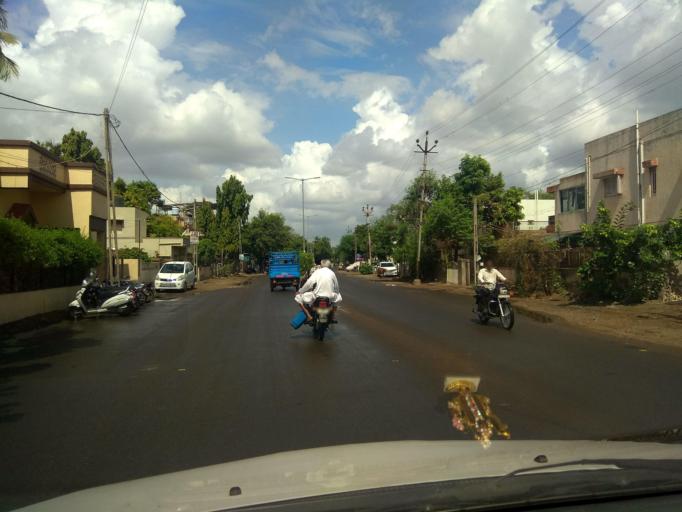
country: IN
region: Gujarat
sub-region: Bhavnagar
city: Bhavnagar
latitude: 21.7436
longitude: 72.1518
